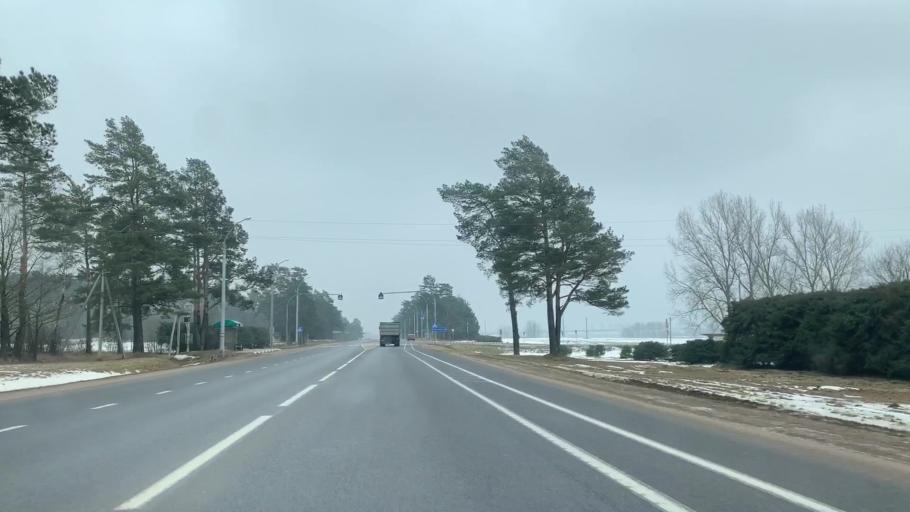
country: BY
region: Minsk
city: Nyasvizh
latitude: 53.2475
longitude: 26.6242
